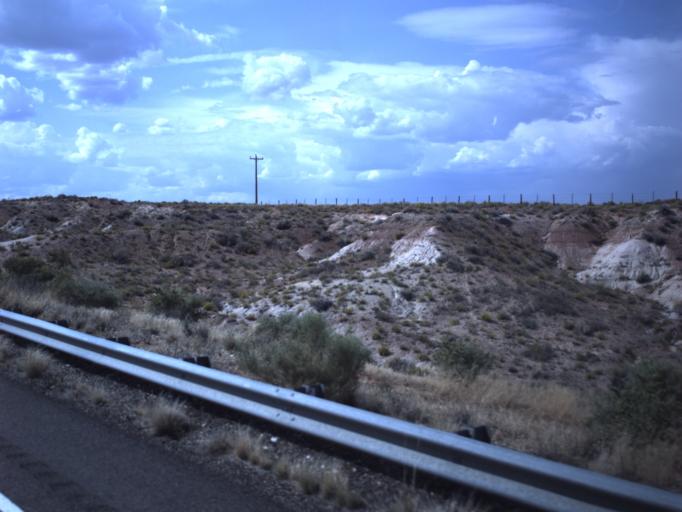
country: US
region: Arizona
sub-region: Coconino County
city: Page
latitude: 37.0998
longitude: -111.7957
